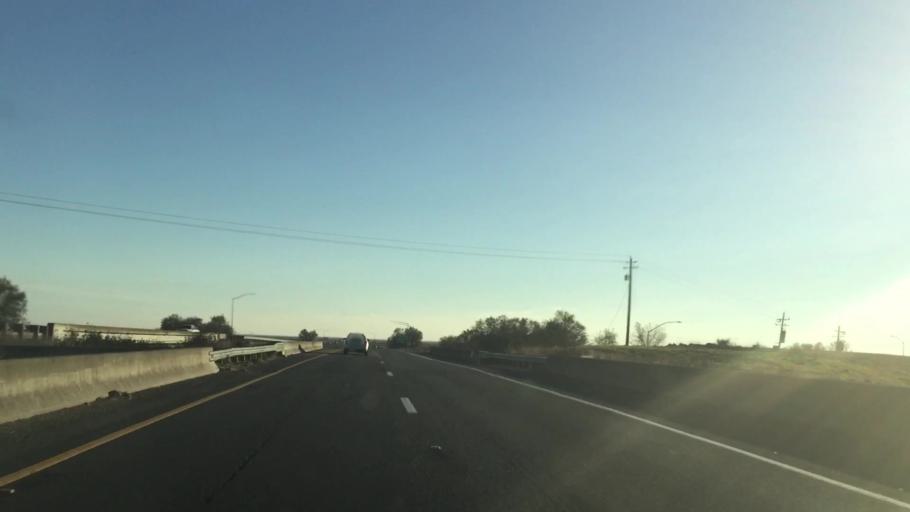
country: US
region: California
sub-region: Sacramento County
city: Elverta
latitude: 38.8209
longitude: -121.5439
